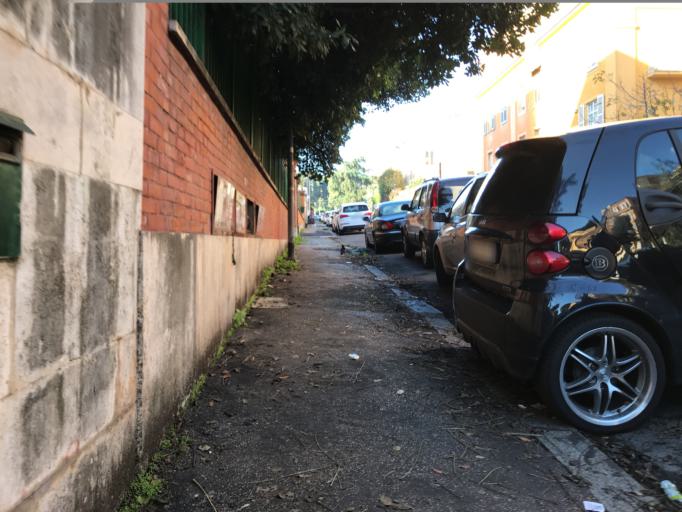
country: IT
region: Latium
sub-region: Citta metropolitana di Roma Capitale
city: Rome
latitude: 41.9113
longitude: 12.5111
